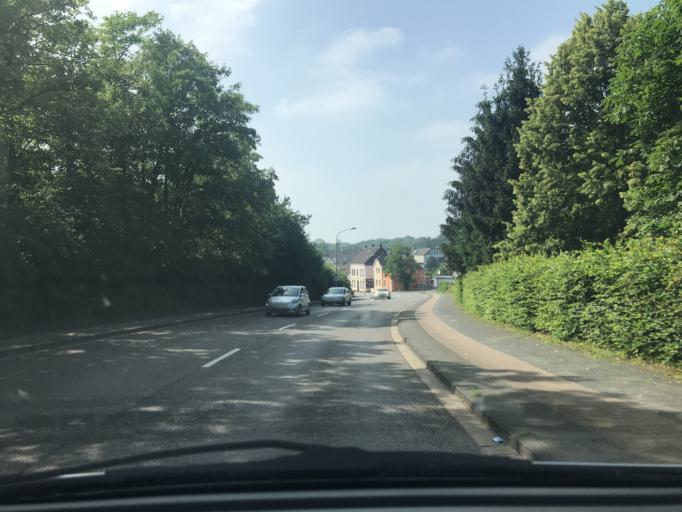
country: DE
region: North Rhine-Westphalia
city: Haan
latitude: 51.1929
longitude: 6.9962
